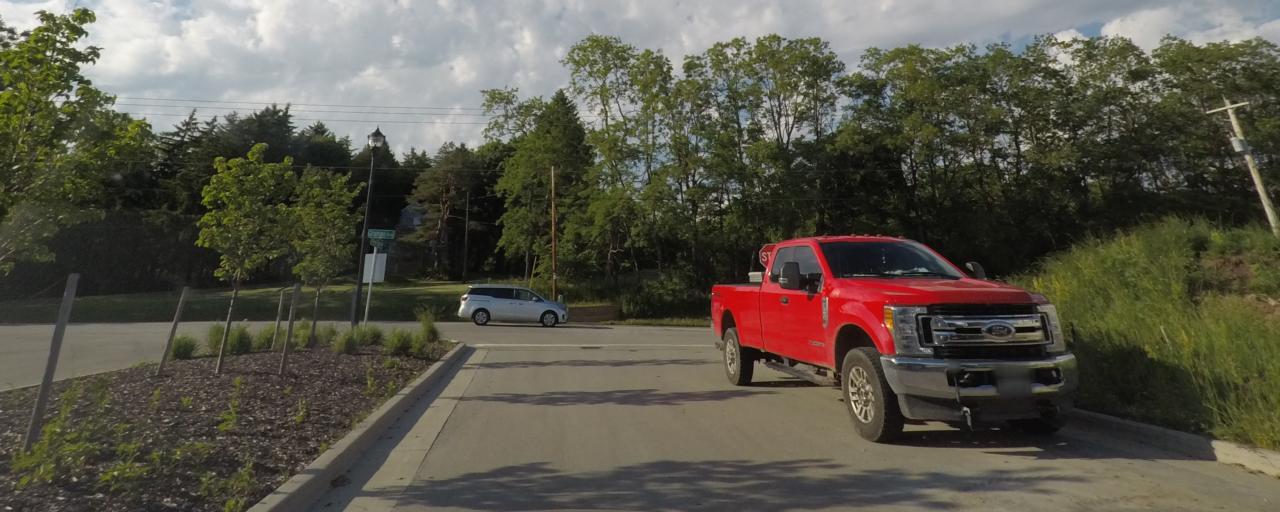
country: US
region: Wisconsin
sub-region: Waukesha County
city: New Berlin
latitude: 42.9440
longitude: -88.0918
